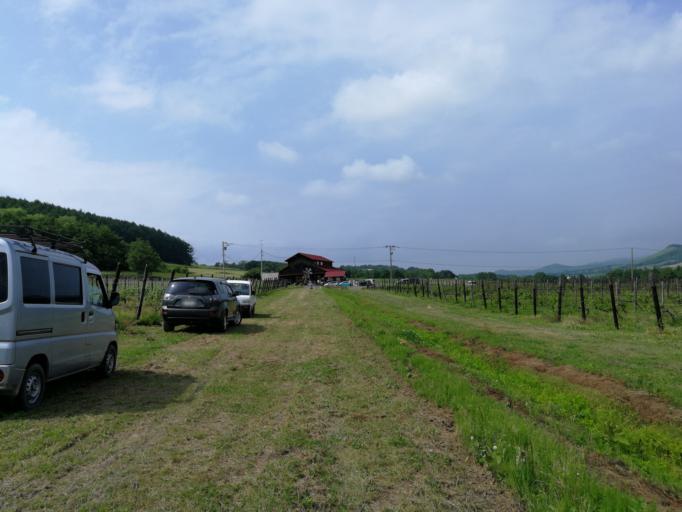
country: JP
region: Hokkaido
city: Iwamizawa
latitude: 43.1915
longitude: 141.8200
